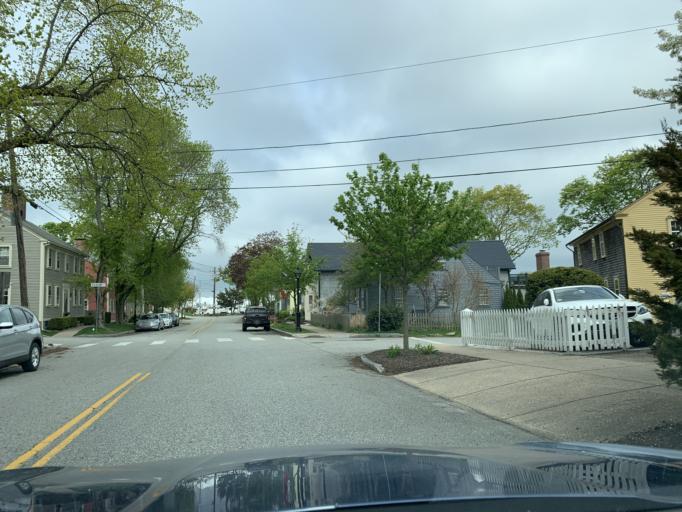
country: US
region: Rhode Island
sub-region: Washington County
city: North Kingstown
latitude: 41.5722
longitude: -71.4476
